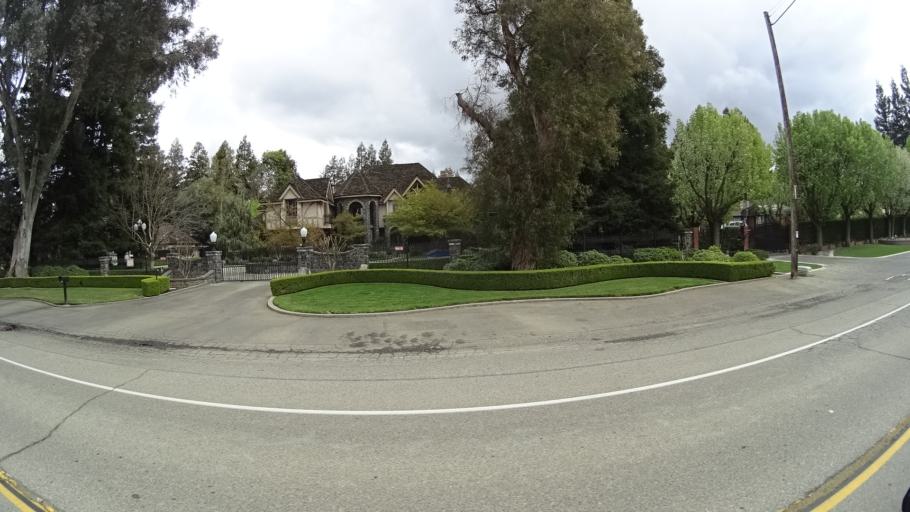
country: US
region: California
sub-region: Fresno County
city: Fresno
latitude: 36.8424
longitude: -119.8354
